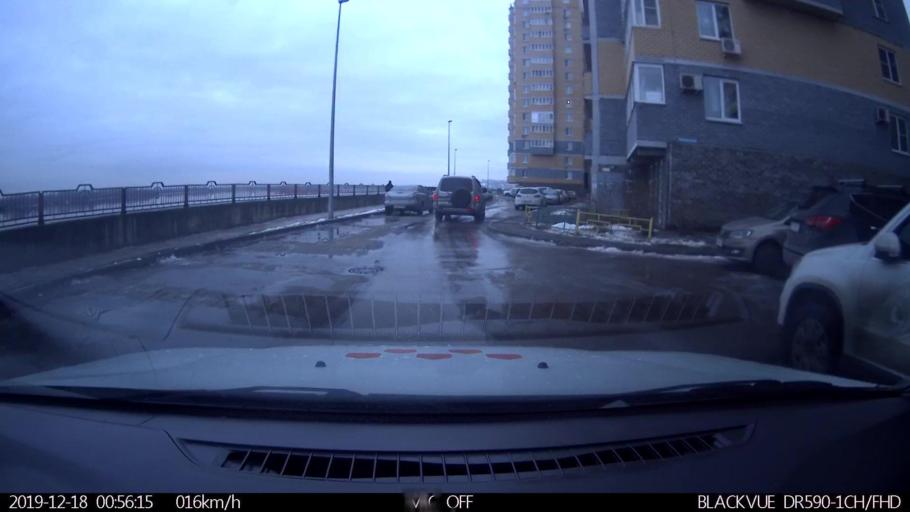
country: RU
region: Nizjnij Novgorod
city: Nizhniy Novgorod
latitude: 56.3494
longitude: 43.9303
